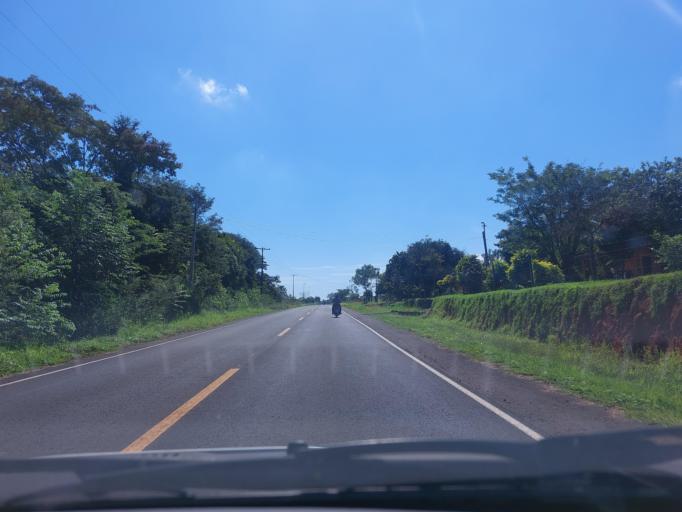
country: PY
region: San Pedro
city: Guayaybi
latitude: -24.5772
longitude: -56.5196
